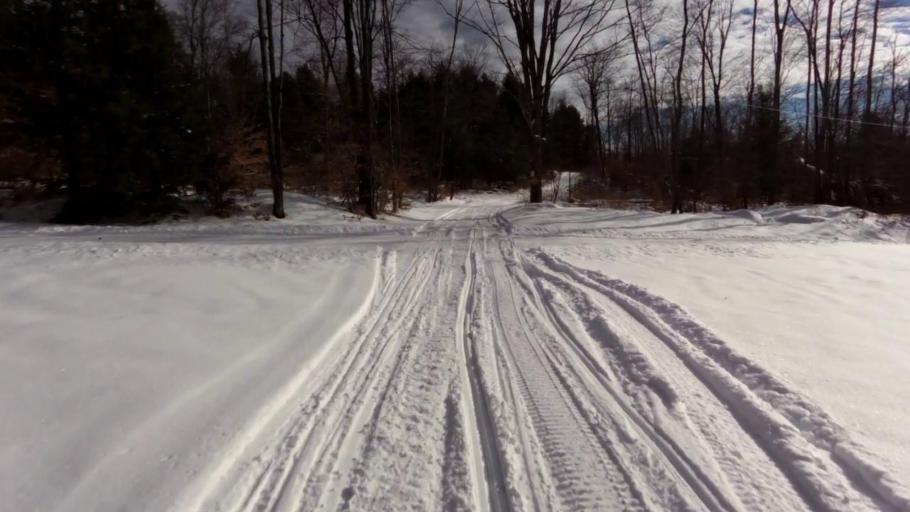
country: US
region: Pennsylvania
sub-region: McKean County
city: Foster Brook
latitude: 42.0049
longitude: -78.5420
